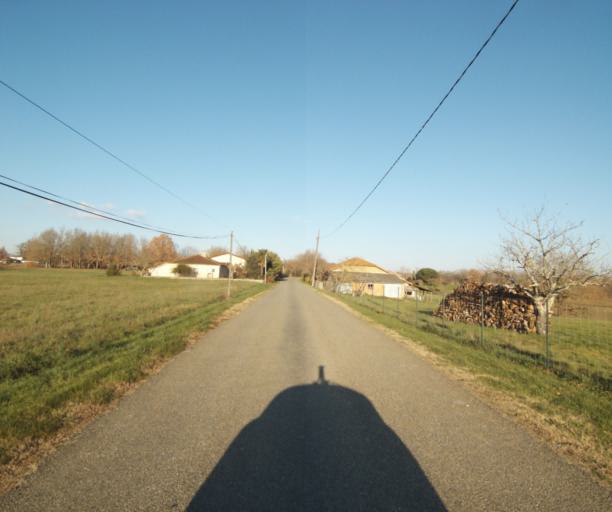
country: FR
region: Midi-Pyrenees
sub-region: Departement du Tarn-et-Garonne
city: Moissac
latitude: 44.1480
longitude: 1.1228
